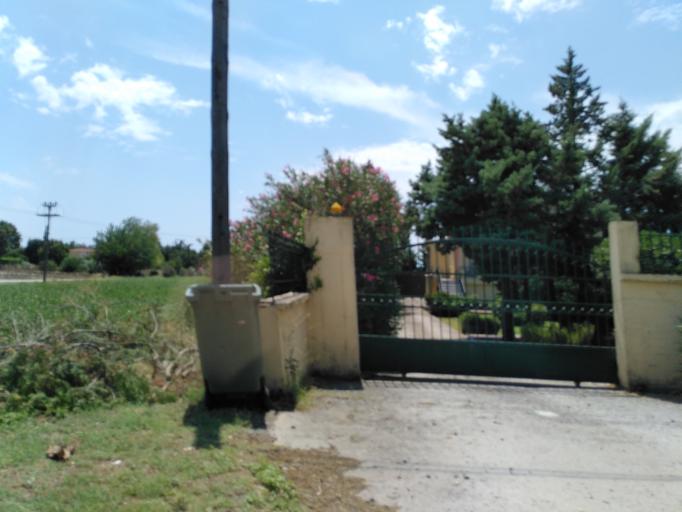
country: GR
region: Central Macedonia
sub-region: Nomos Thessalonikis
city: Epanomi
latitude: 40.4316
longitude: 22.9166
